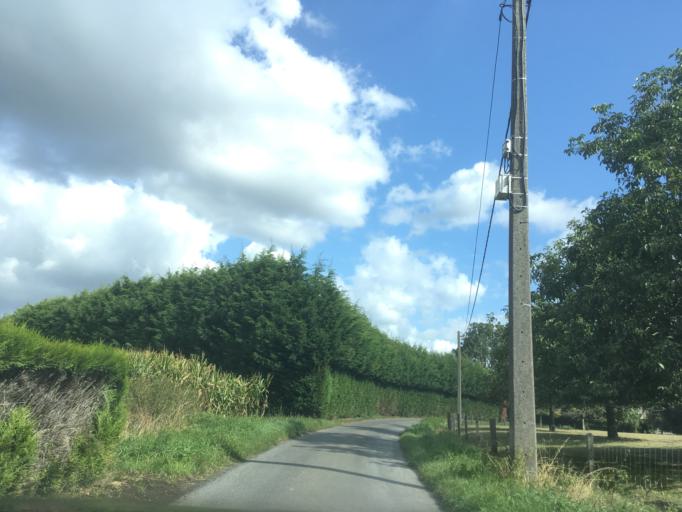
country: BE
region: Flanders
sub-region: Provincie West-Vlaanderen
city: Kortemark
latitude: 51.0131
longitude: 3.0334
